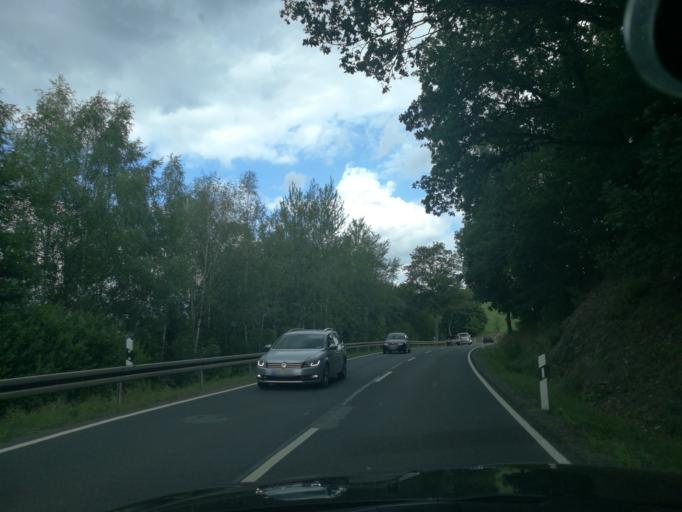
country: DE
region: Saxony
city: Oelsnitz
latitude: 50.3974
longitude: 12.1876
